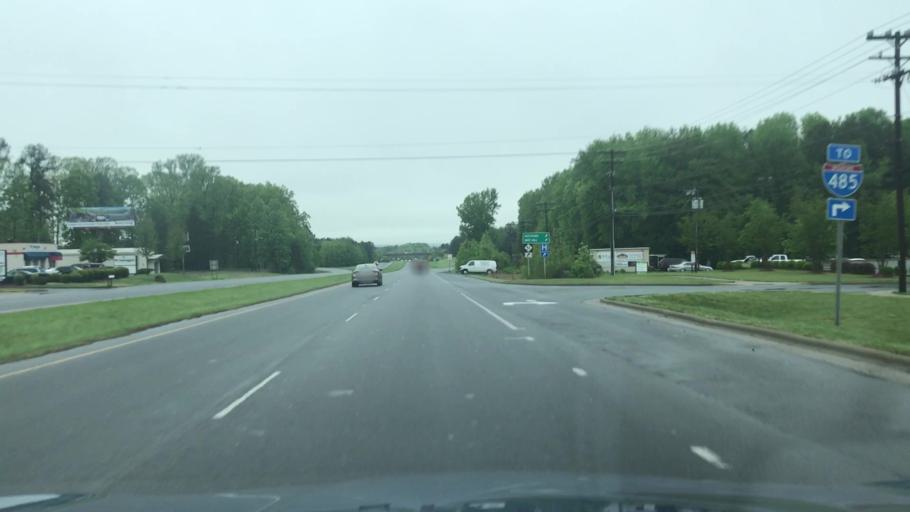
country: US
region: North Carolina
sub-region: Mecklenburg County
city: Matthews
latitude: 35.1207
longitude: -80.6998
